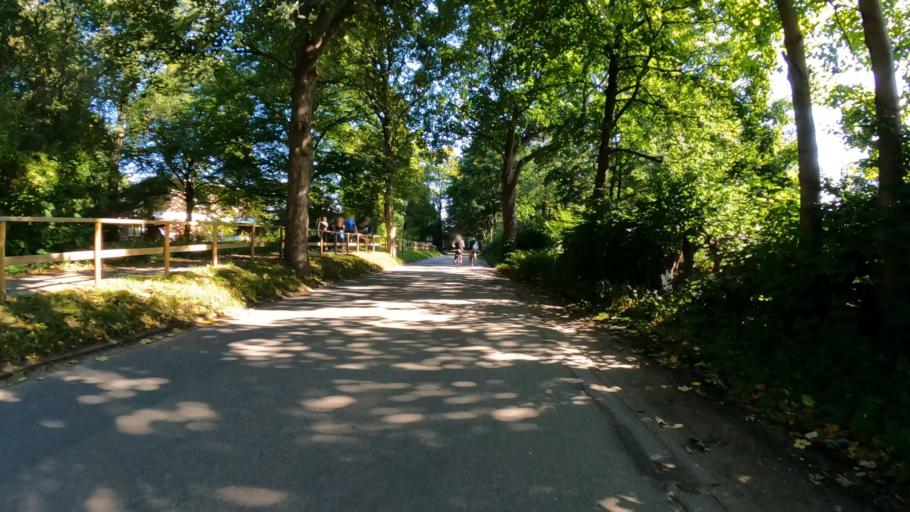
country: DE
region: Schleswig-Holstein
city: Ahrensburg
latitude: 53.6605
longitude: 10.1941
